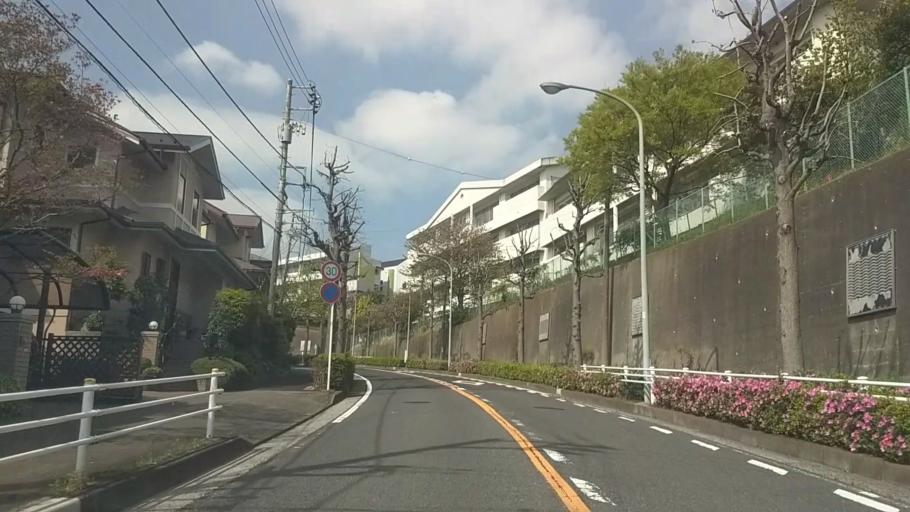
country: JP
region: Kanagawa
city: Yokohama
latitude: 35.3718
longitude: 139.6213
